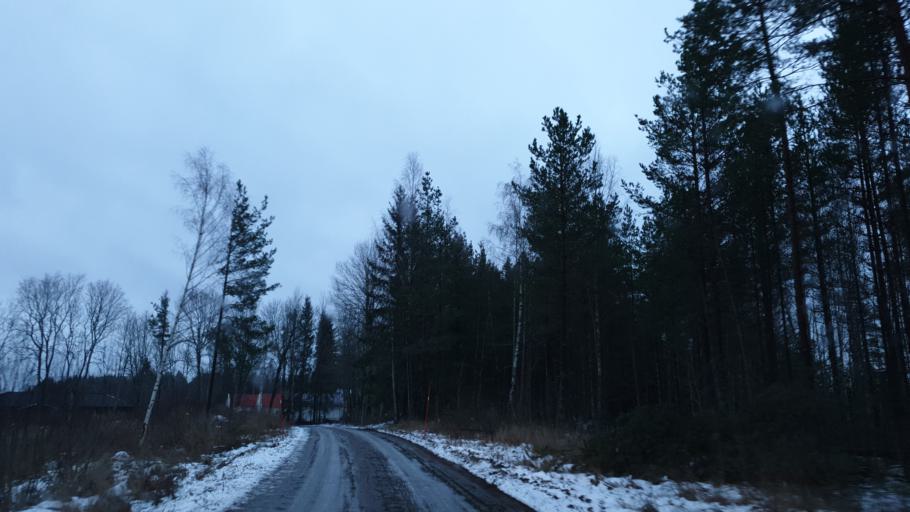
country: SE
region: Uppsala
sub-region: Tierps Kommun
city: Tierp
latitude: 60.3441
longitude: 17.4687
